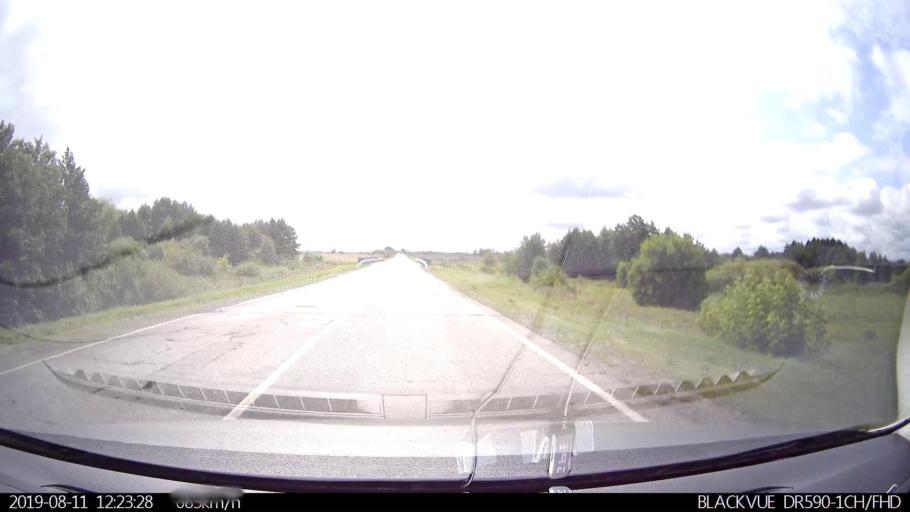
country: RU
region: Ulyanovsk
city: Ignatovka
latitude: 53.8949
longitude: 47.9504
